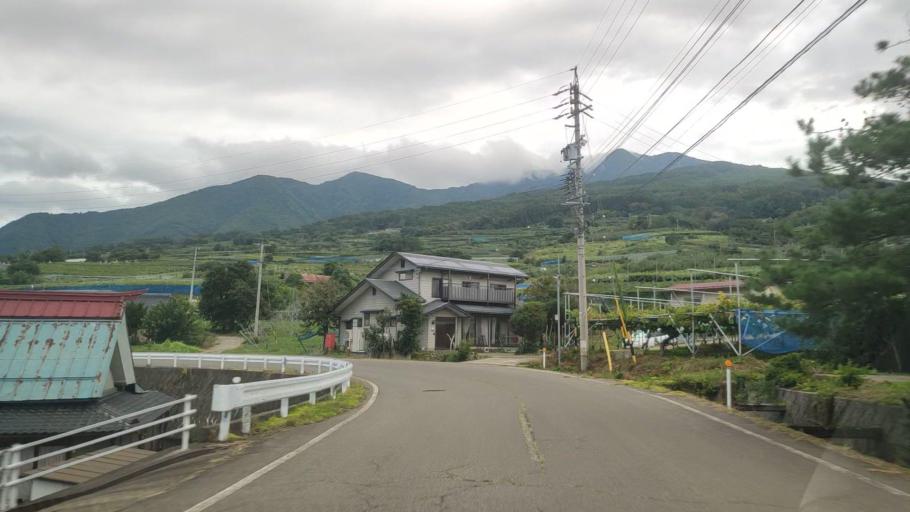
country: JP
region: Nagano
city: Nakano
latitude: 36.7780
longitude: 138.3755
